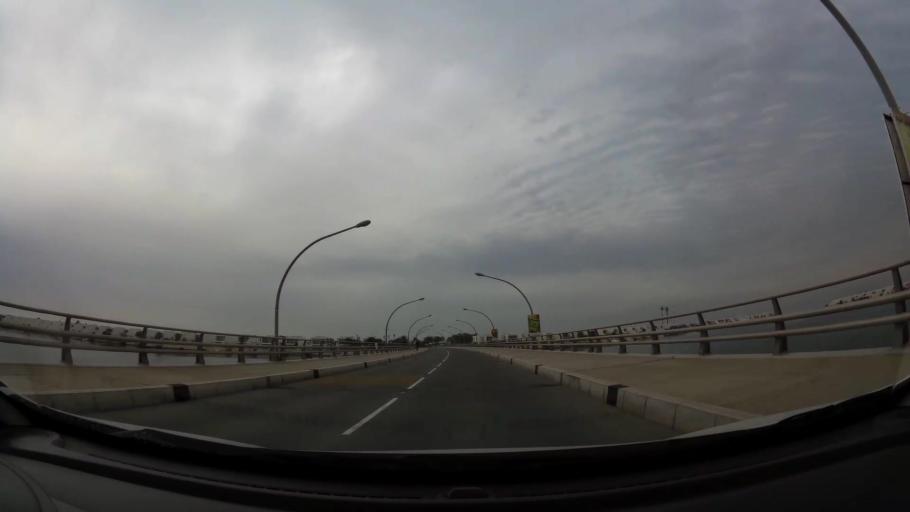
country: BH
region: Central Governorate
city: Dar Kulayb
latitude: 25.8356
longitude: 50.6148
